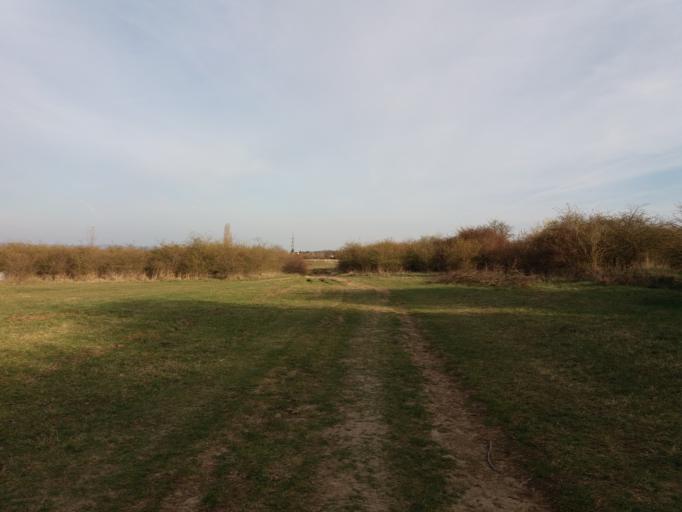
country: HU
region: Pest
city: Pomaz
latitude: 47.6234
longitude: 19.0232
